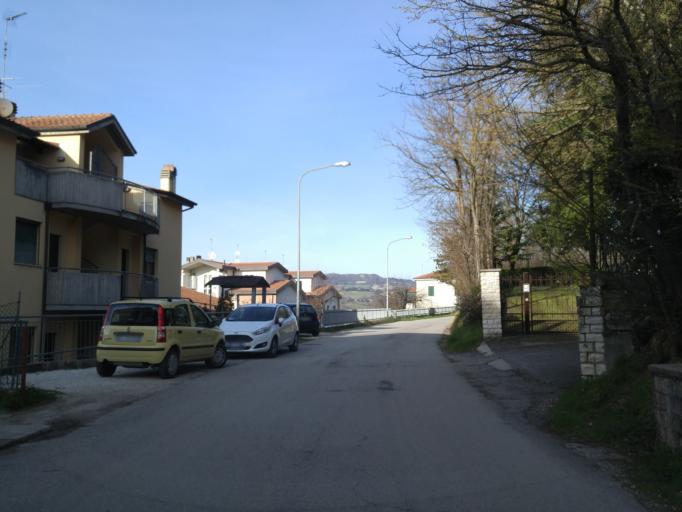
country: IT
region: The Marches
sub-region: Provincia di Pesaro e Urbino
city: Fermignano
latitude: 43.6786
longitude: 12.6476
